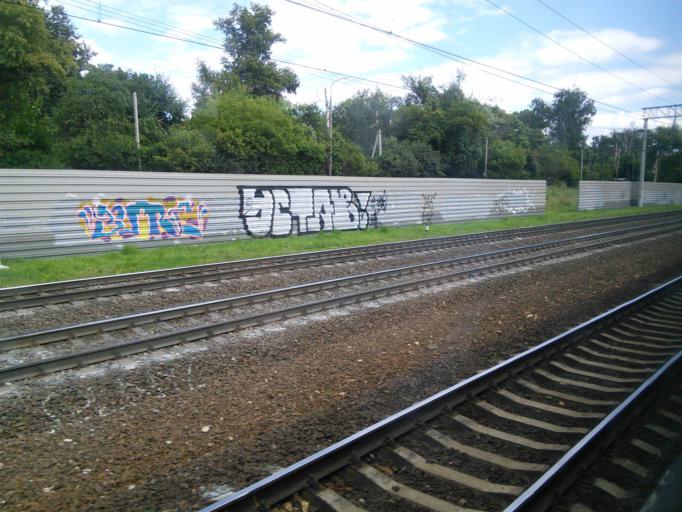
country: RU
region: Moscow
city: Zhulebino
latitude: 55.7022
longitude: 37.8567
